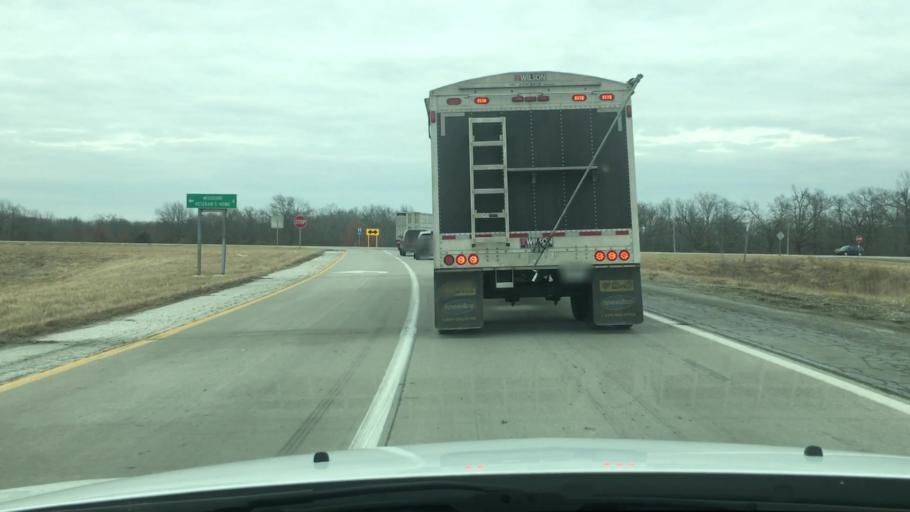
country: US
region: Missouri
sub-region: Audrain County
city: Mexico
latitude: 39.1624
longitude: -91.8412
